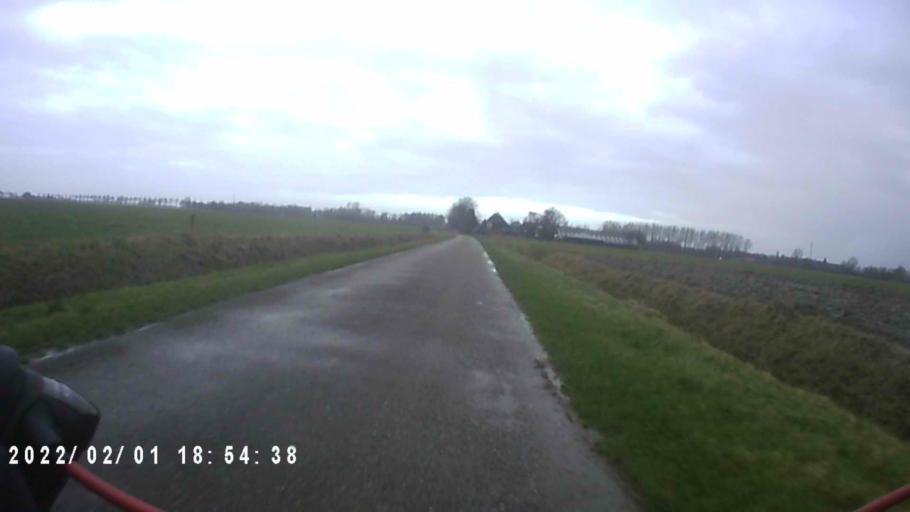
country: NL
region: Groningen
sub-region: Gemeente Zuidhorn
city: Oldehove
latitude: 53.3520
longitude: 6.4128
